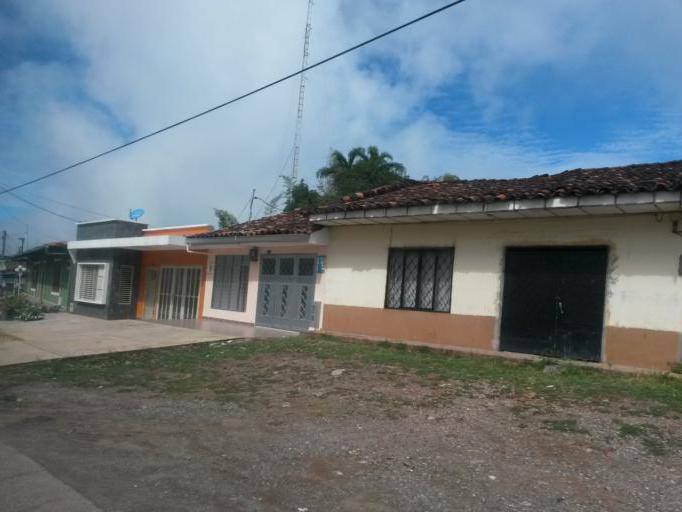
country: CO
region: Cauca
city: El Bordo
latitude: 2.1177
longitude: -76.9834
